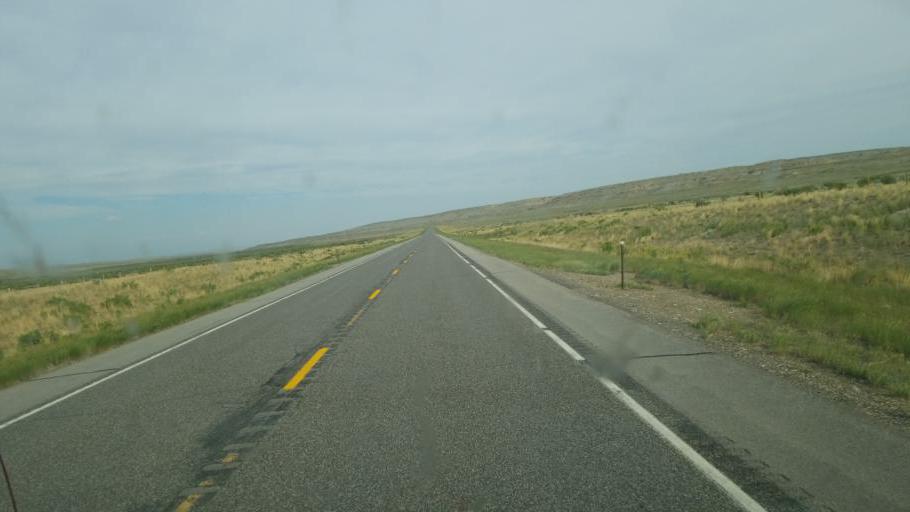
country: US
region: Wyoming
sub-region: Fremont County
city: Riverton
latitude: 43.2152
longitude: -107.9519
